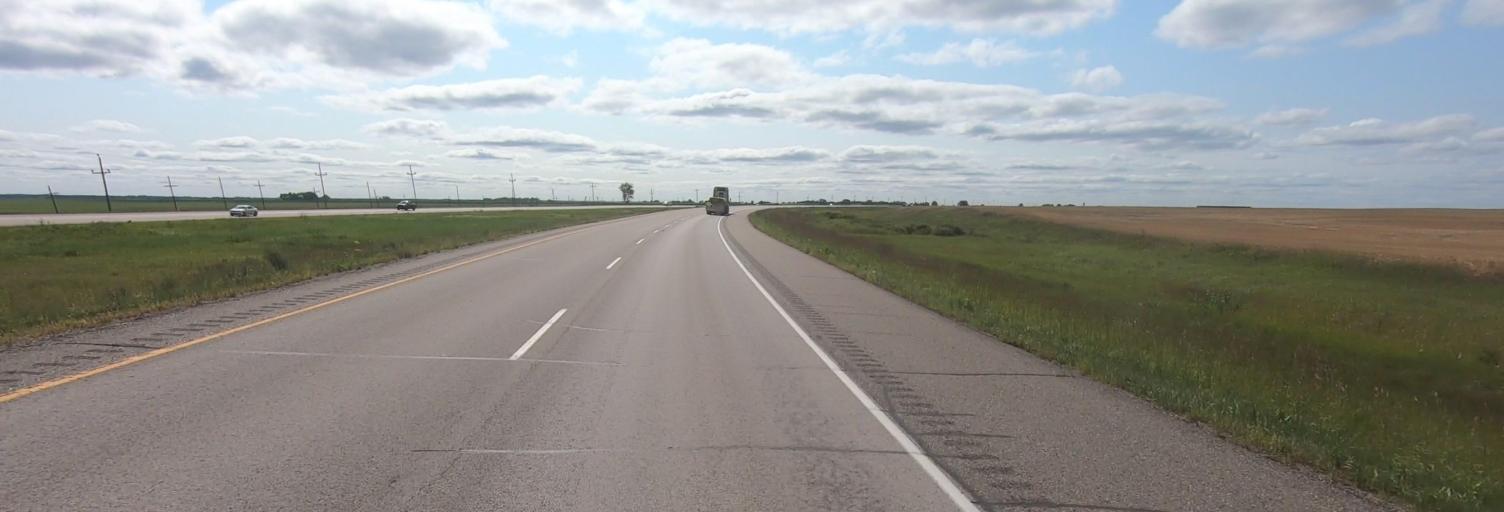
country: CA
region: Manitoba
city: Souris
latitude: 49.7853
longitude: -100.4271
